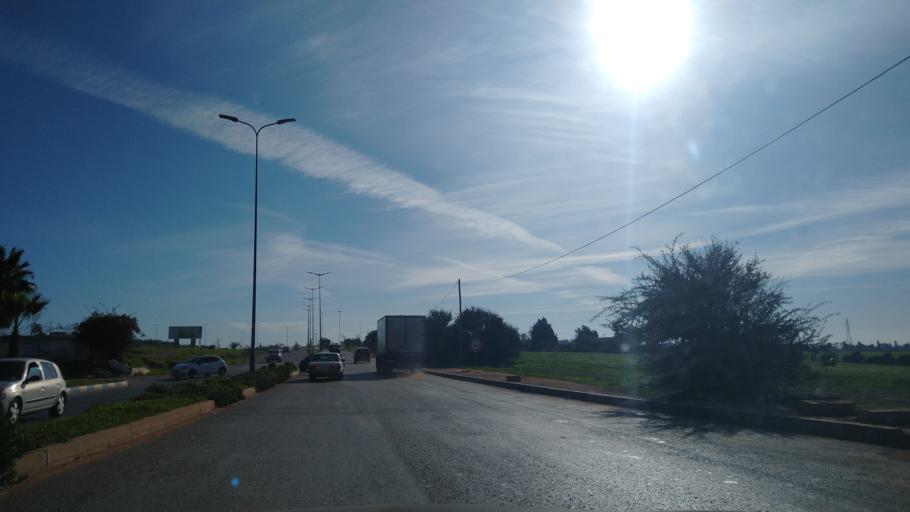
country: MA
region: Rabat-Sale-Zemmour-Zaer
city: Sale
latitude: 33.9868
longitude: -6.7395
